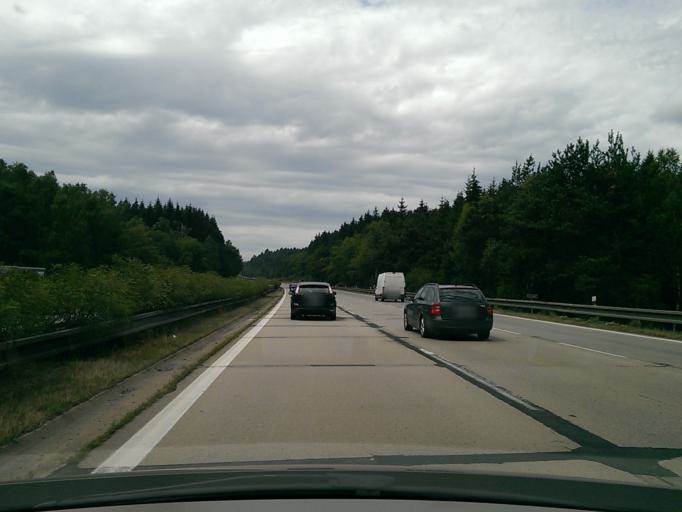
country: CZ
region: Vysocina
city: Kamenice
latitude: 49.4073
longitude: 15.8087
